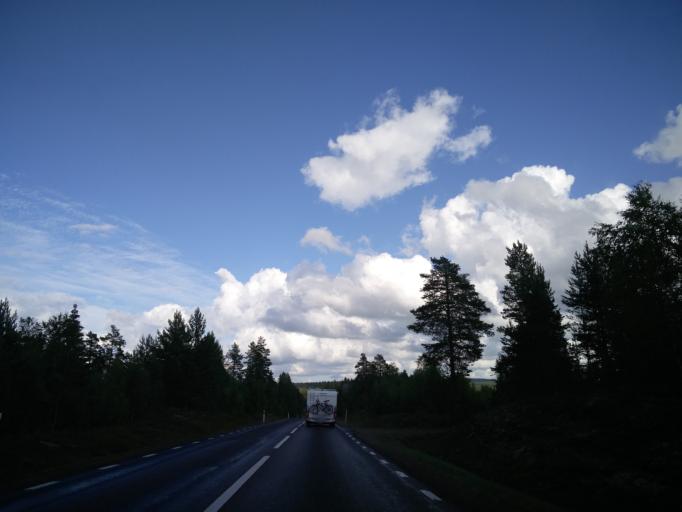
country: SE
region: Vaermland
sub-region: Hagfors Kommun
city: Ekshaerad
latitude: 60.4785
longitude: 13.3599
